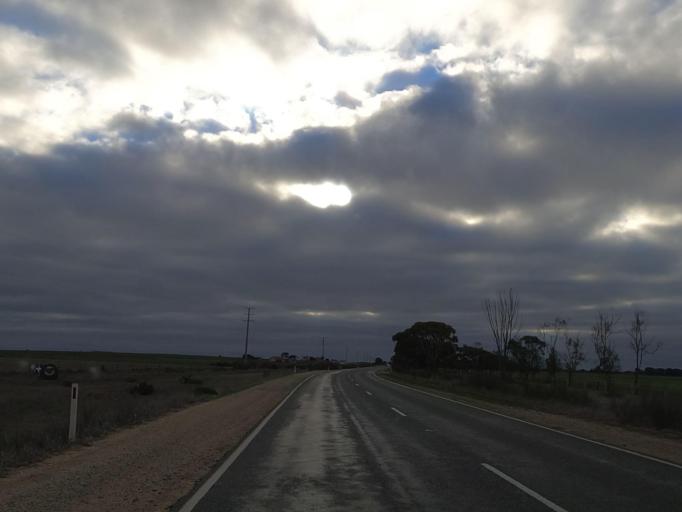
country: AU
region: Victoria
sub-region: Swan Hill
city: Swan Hill
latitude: -35.6472
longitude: 143.8362
